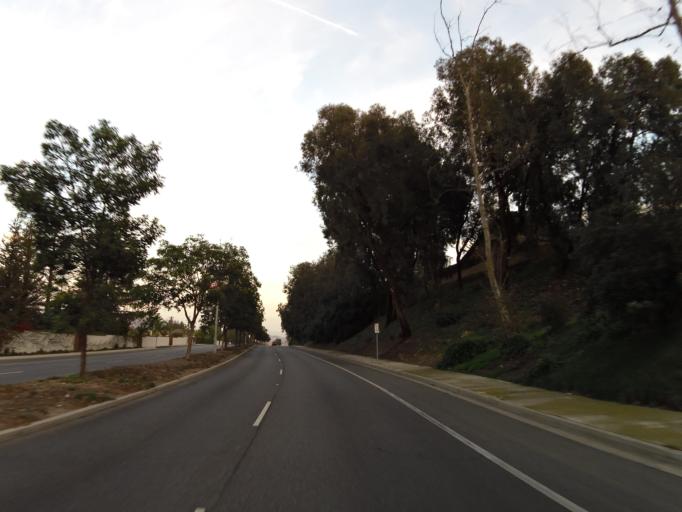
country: US
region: California
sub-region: Ventura County
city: Moorpark
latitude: 34.2617
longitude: -118.8723
